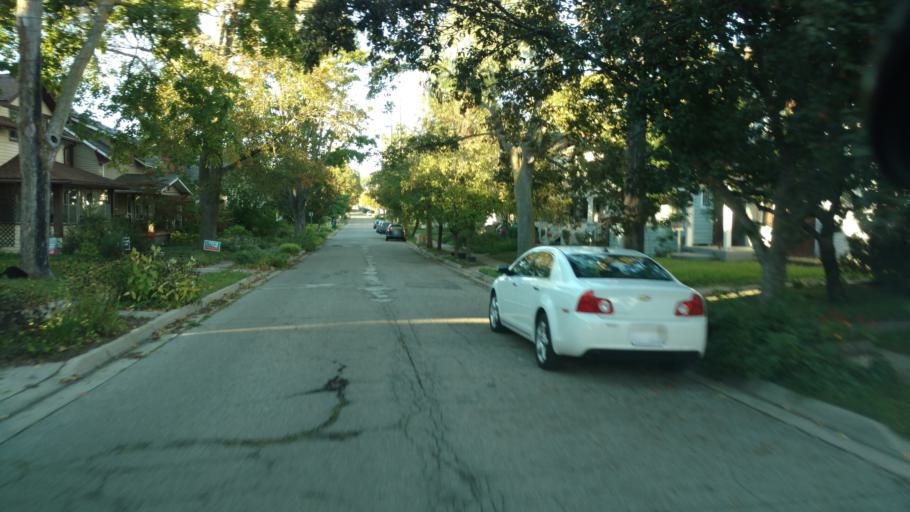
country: US
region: Michigan
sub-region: Ingham County
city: Lansing
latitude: 42.7313
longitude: -84.5249
